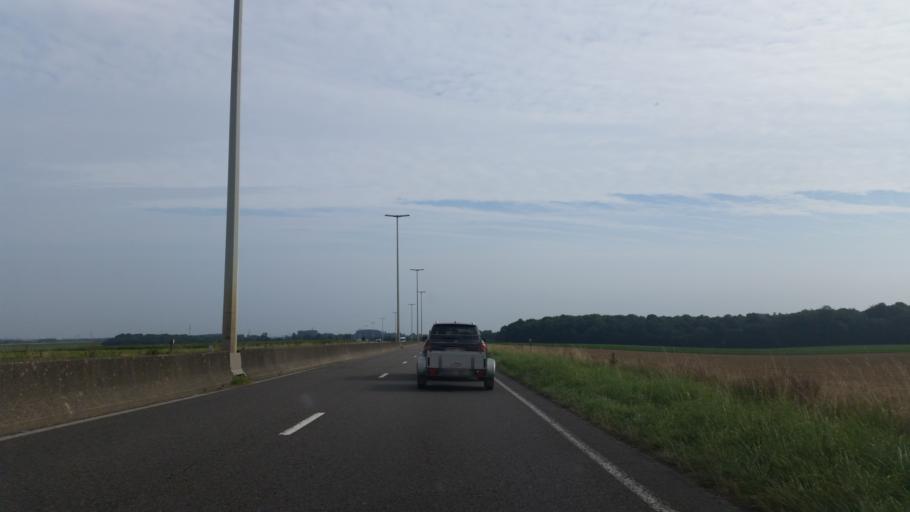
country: BE
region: Wallonia
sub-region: Province de Liege
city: Nandrin
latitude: 50.5316
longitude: 5.4339
